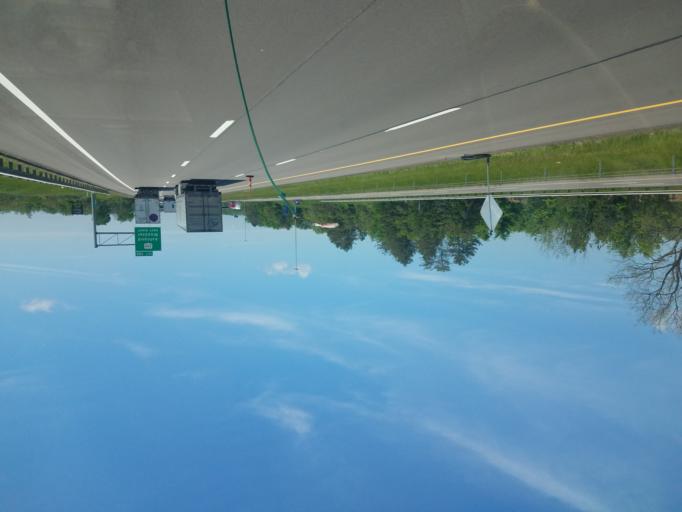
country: US
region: Ohio
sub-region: Ashland County
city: Ashland
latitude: 40.8493
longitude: -82.2665
